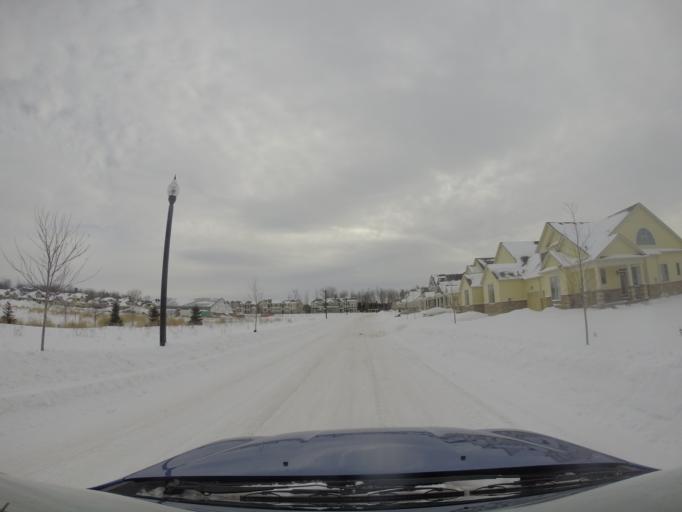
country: CA
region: Ontario
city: Wasaga Beach
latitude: 44.5283
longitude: -80.0103
